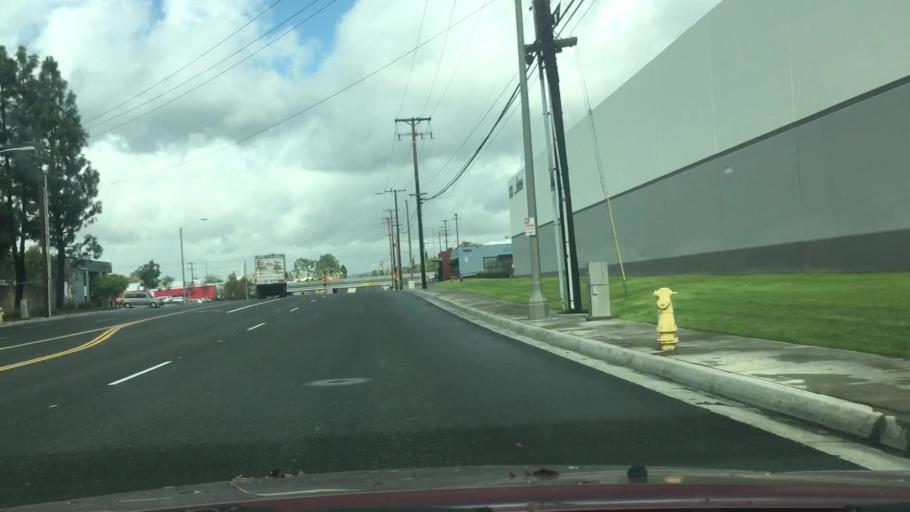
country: US
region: California
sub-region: Los Angeles County
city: La Mirada
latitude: 33.8954
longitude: -118.0290
